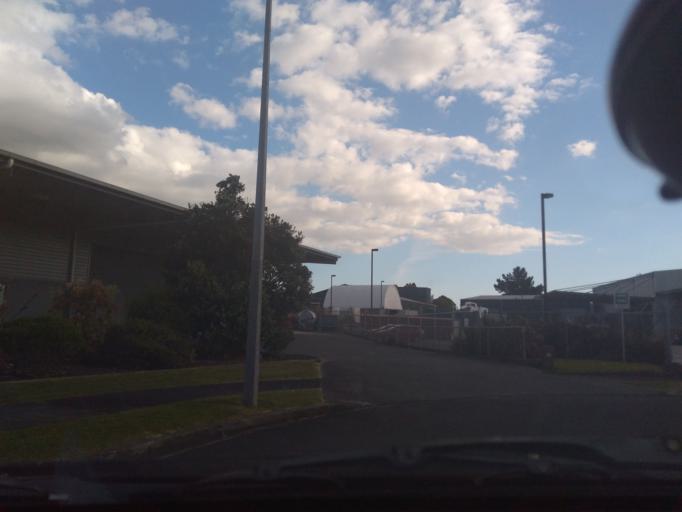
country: NZ
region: Auckland
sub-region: Auckland
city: Manukau City
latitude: -36.9430
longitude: 174.8854
